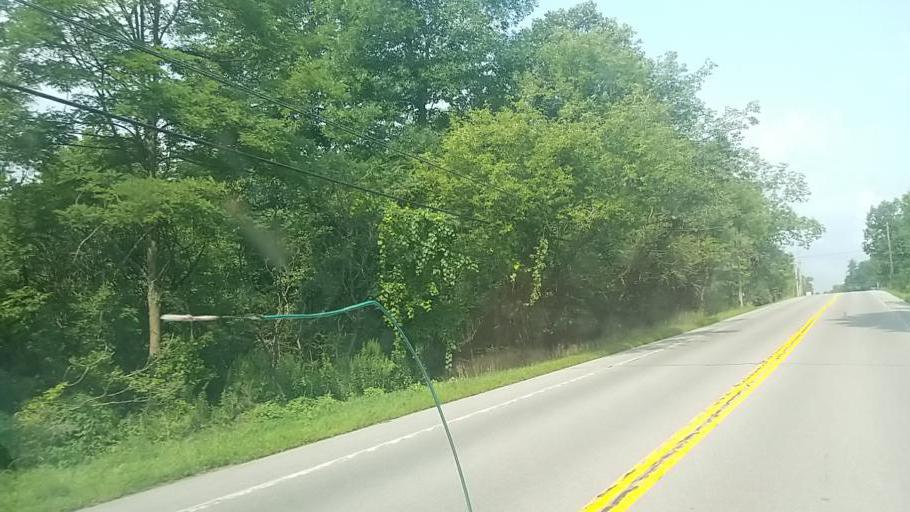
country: US
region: New York
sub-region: Montgomery County
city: Saint Johnsville
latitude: 42.9787
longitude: -74.6391
